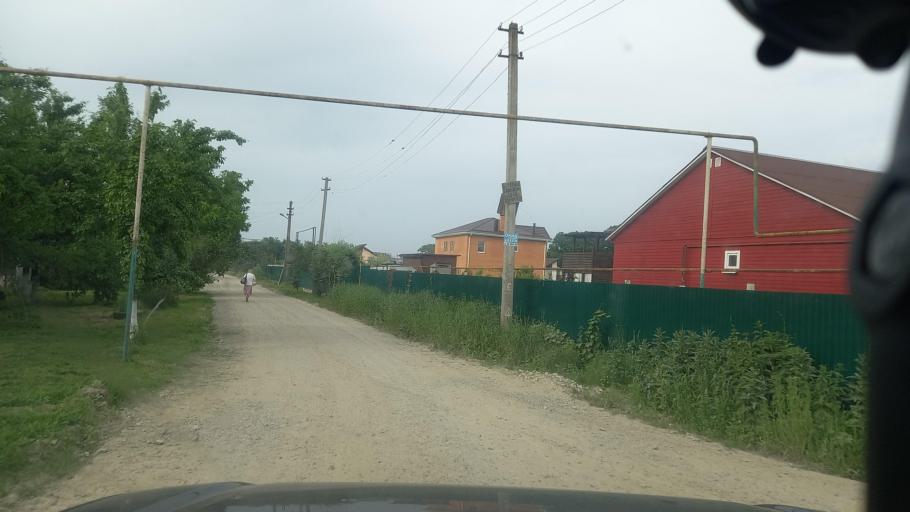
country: RU
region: Krasnodarskiy
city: Saratovskaya
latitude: 44.7517
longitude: 39.2453
